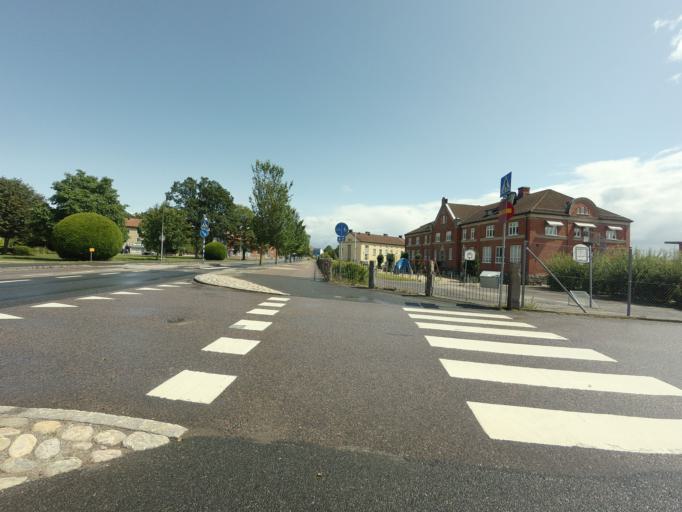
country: SE
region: Skane
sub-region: Osby Kommun
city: Osby
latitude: 56.3790
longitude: 13.9959
